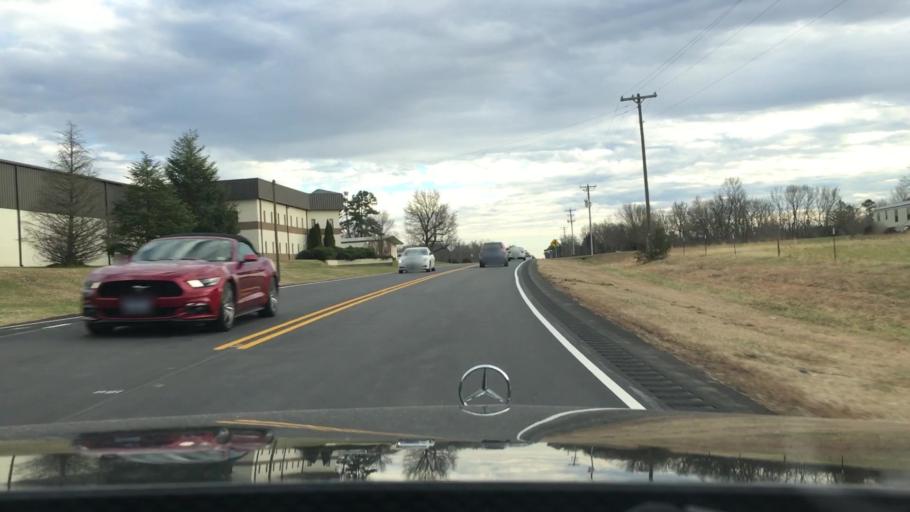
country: US
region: North Carolina
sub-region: Alamance County
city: Mebane
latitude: 36.2692
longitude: -79.1977
